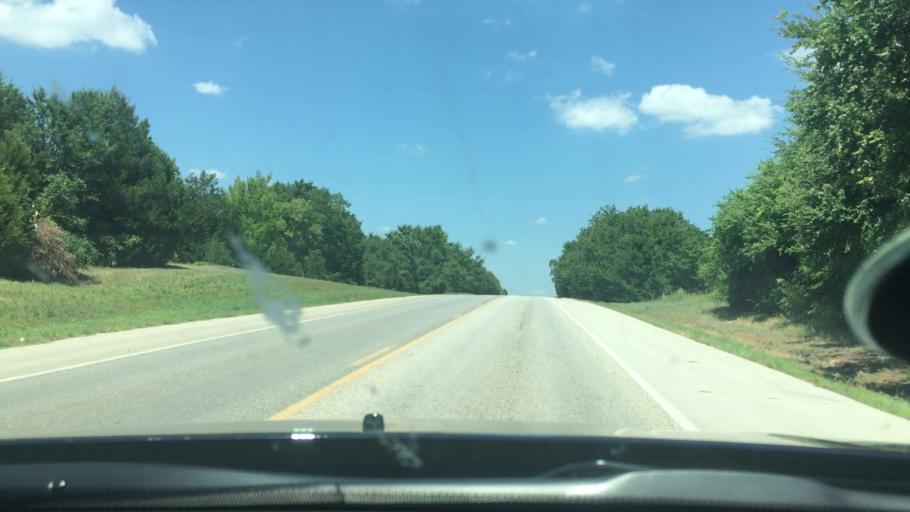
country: US
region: Oklahoma
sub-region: Marshall County
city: Oakland
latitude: 34.1780
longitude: -96.8618
